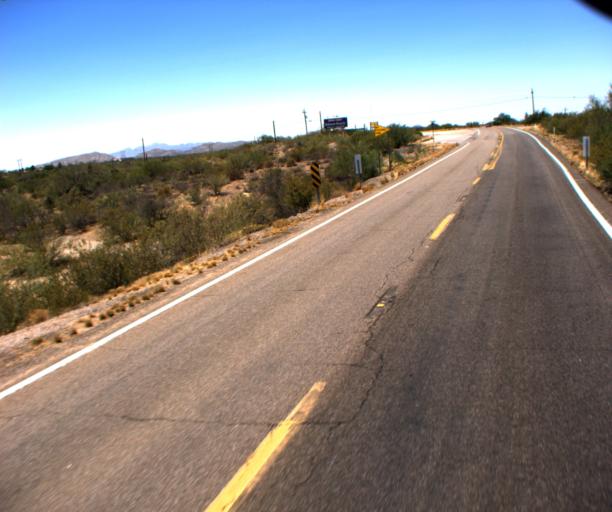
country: US
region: Arizona
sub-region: Pima County
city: Catalina
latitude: 32.6525
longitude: -111.0331
